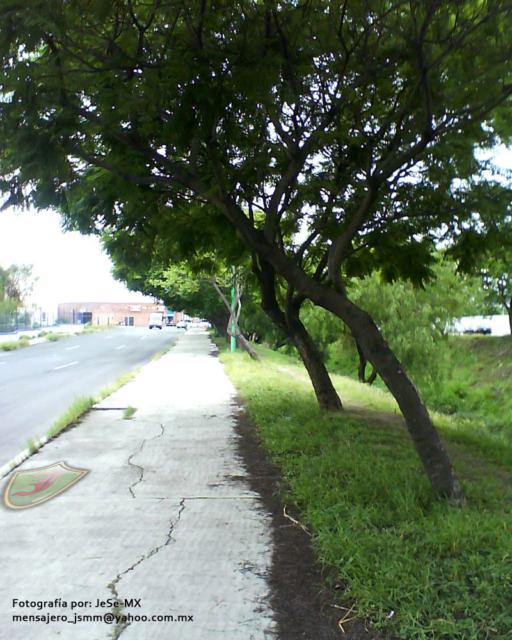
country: MX
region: Queretaro
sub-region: Queretaro
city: Santiago de Queretaro
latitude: 20.6108
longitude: -100.4077
